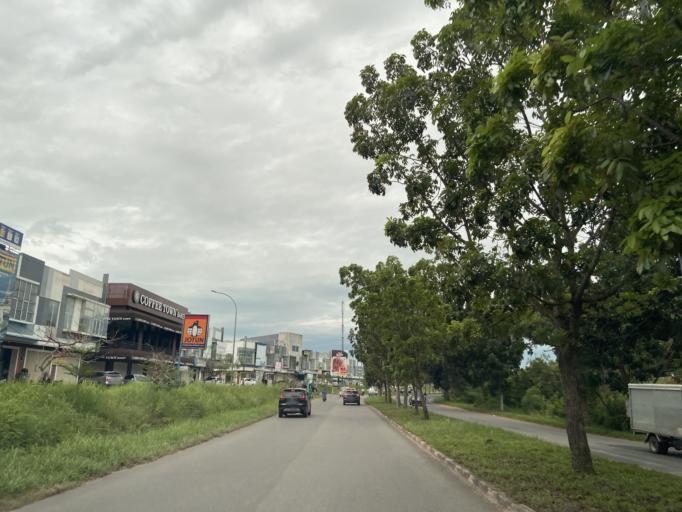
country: SG
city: Singapore
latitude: 1.1155
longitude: 104.0595
